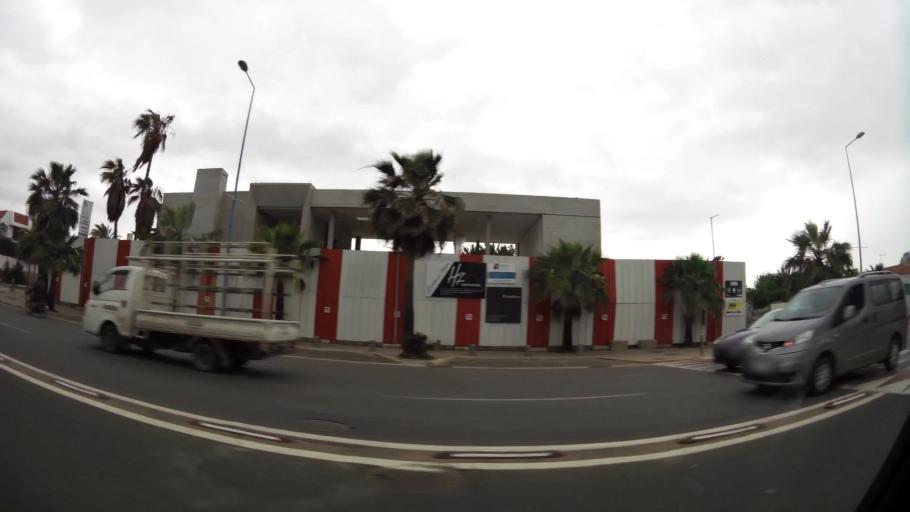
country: MA
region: Grand Casablanca
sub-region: Casablanca
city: Casablanca
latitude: 33.5927
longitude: -7.6747
